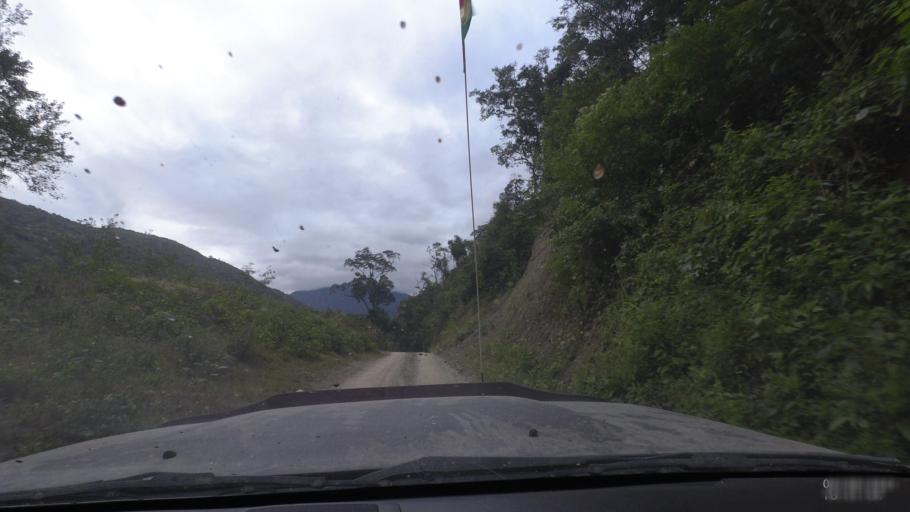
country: BO
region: La Paz
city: Quime
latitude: -16.5237
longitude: -66.7540
